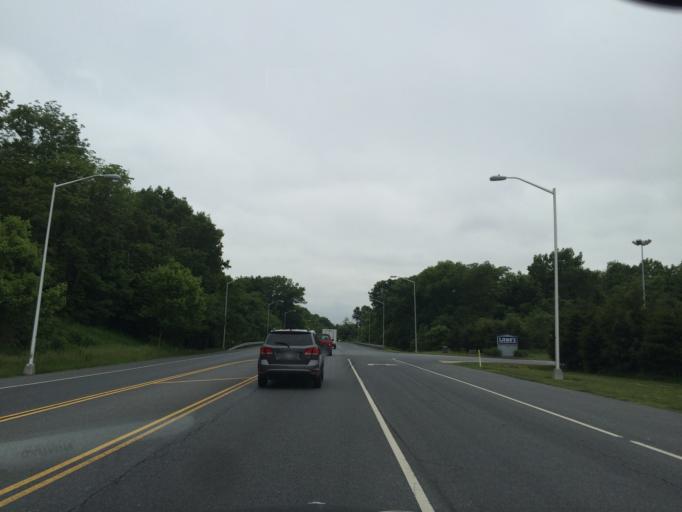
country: US
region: Maryland
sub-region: Washington County
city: Halfway
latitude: 39.6375
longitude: -77.7456
